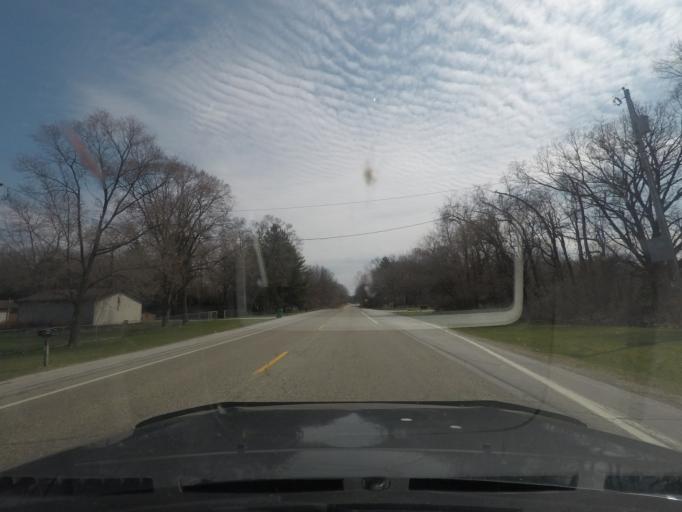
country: US
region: Indiana
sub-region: LaPorte County
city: Trail Creek
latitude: 41.6873
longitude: -86.7985
